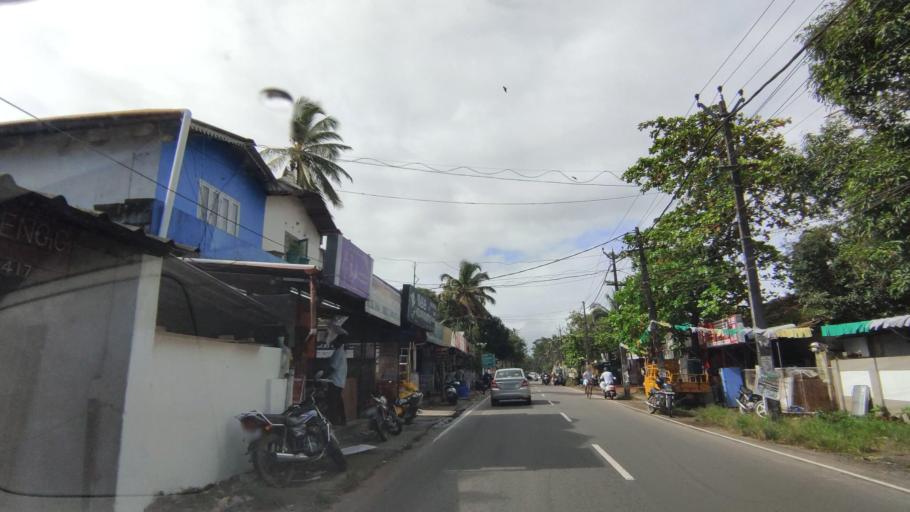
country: IN
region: Kerala
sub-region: Alappuzha
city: Alleppey
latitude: 9.5256
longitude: 76.3402
